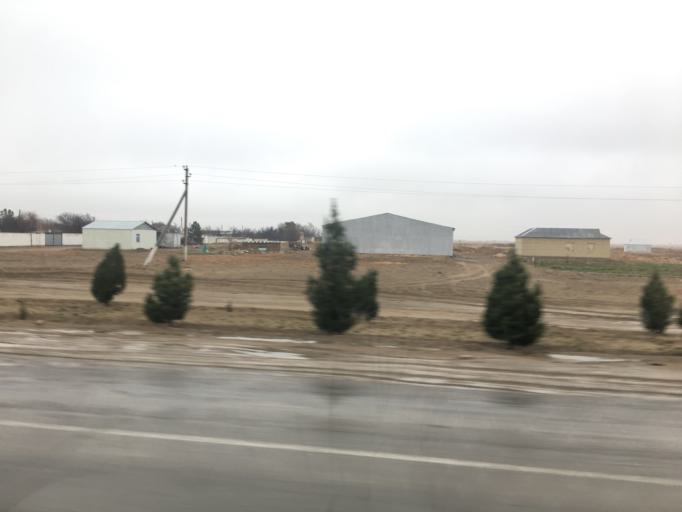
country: TM
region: Mary
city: Mary
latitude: 37.5235
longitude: 61.7266
